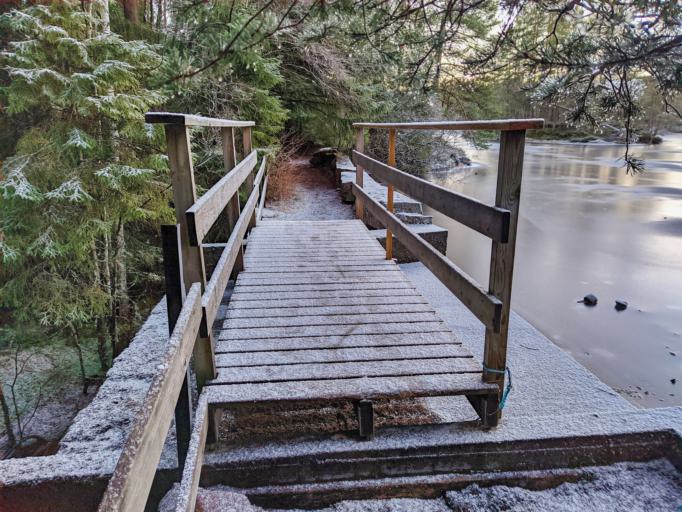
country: NO
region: Akershus
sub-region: Nannestad
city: Teigebyen
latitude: 60.1733
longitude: 10.9809
